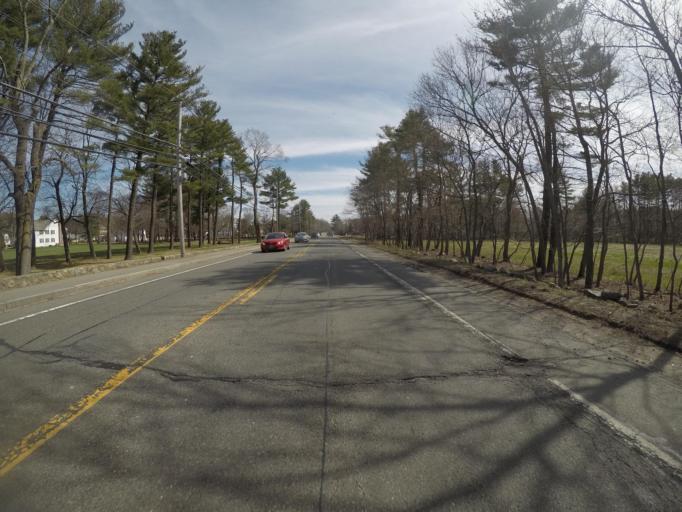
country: US
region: Massachusetts
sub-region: Bristol County
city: Easton
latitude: 42.0568
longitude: -71.0864
